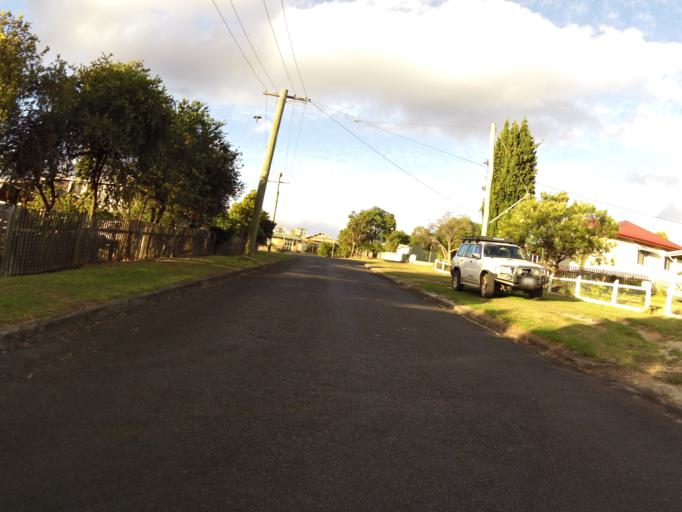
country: AU
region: Western Australia
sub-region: Manjimup
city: Pemberton
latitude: -34.4472
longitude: 116.0340
